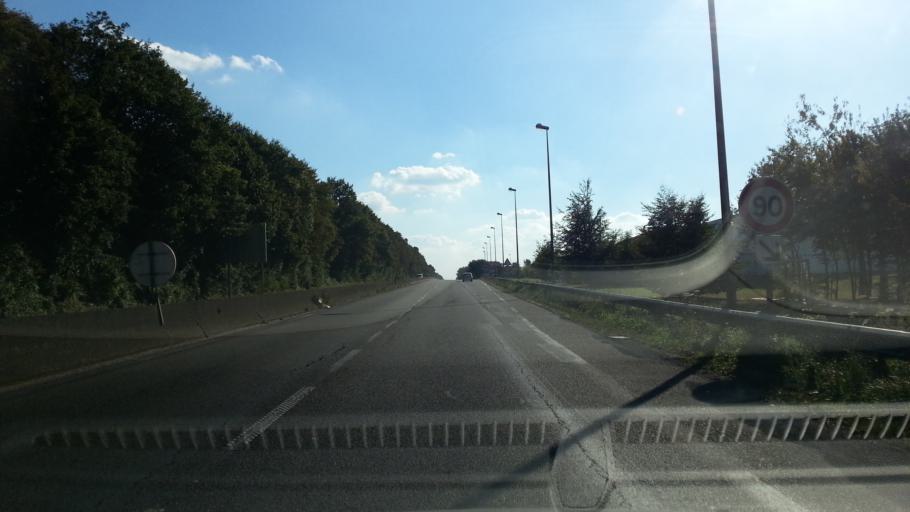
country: FR
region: Picardie
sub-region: Departement de l'Oise
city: Creil
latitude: 49.2425
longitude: 2.4741
